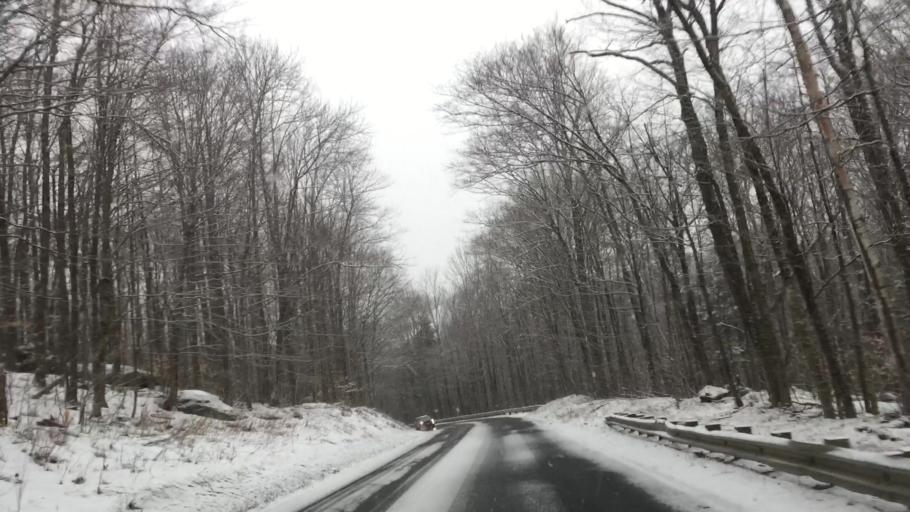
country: US
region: Massachusetts
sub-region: Berkshire County
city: Dalton
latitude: 42.4179
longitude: -73.1839
